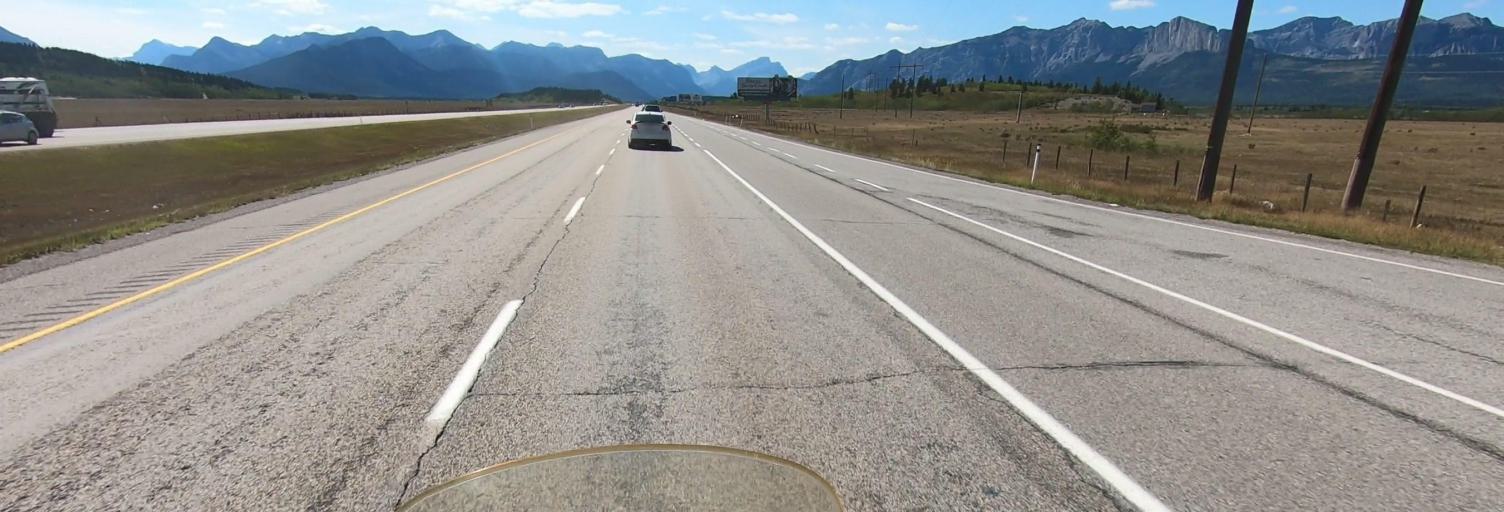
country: CA
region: Alberta
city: Canmore
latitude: 51.1220
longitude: -114.9729
